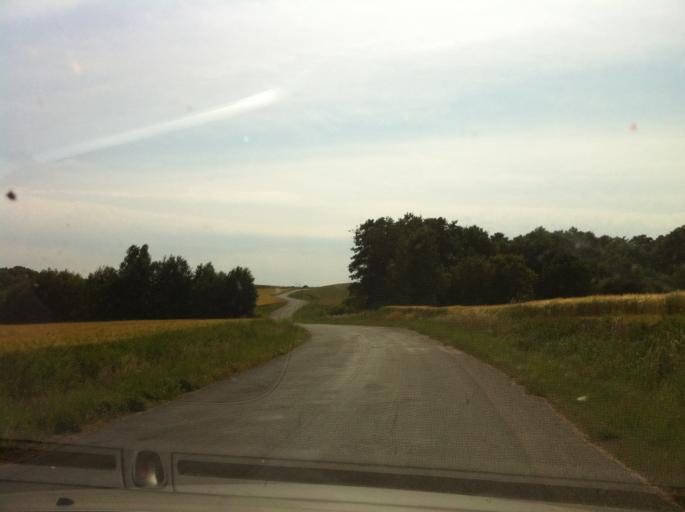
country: SE
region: Skane
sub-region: Eslovs Kommun
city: Stehag
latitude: 55.9673
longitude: 13.3498
